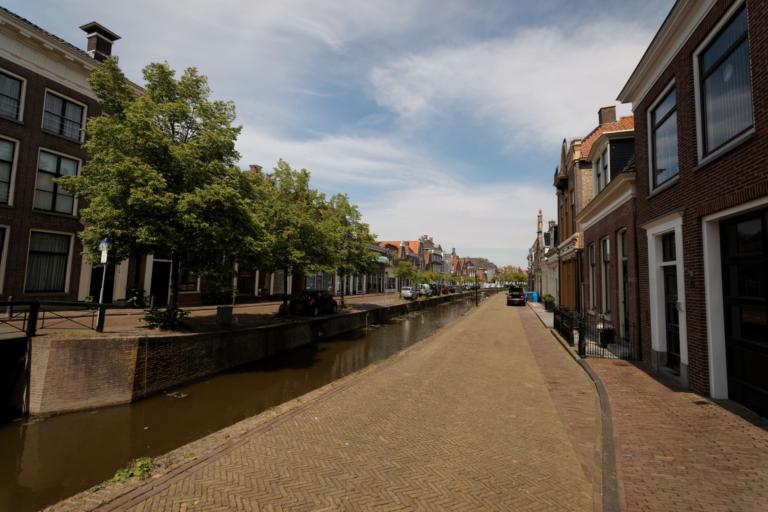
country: NL
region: Friesland
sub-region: Sudwest Fryslan
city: Bolsward
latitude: 53.0635
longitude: 5.5237
